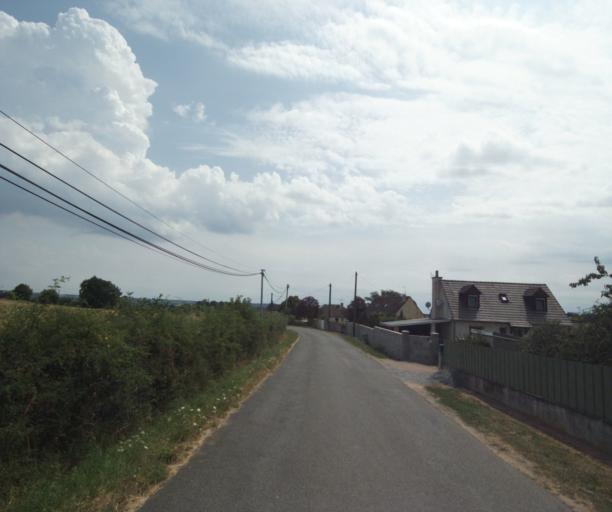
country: FR
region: Bourgogne
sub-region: Departement de Saone-et-Loire
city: Gueugnon
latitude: 46.5970
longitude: 4.0268
